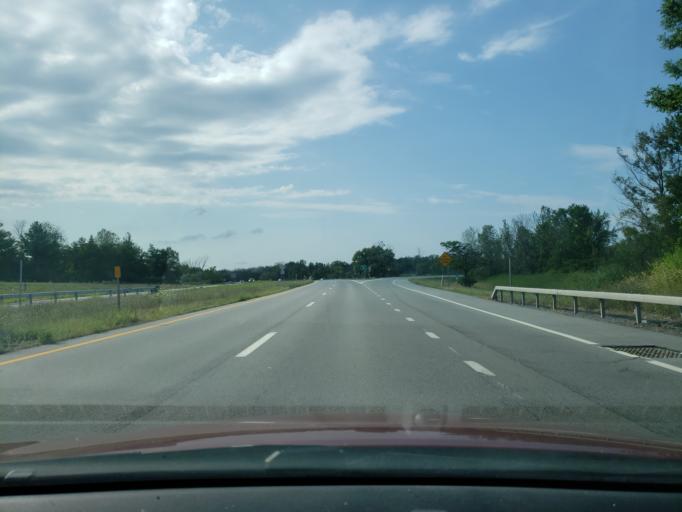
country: US
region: New York
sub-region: Monroe County
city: Greece
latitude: 43.2698
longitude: -77.6639
